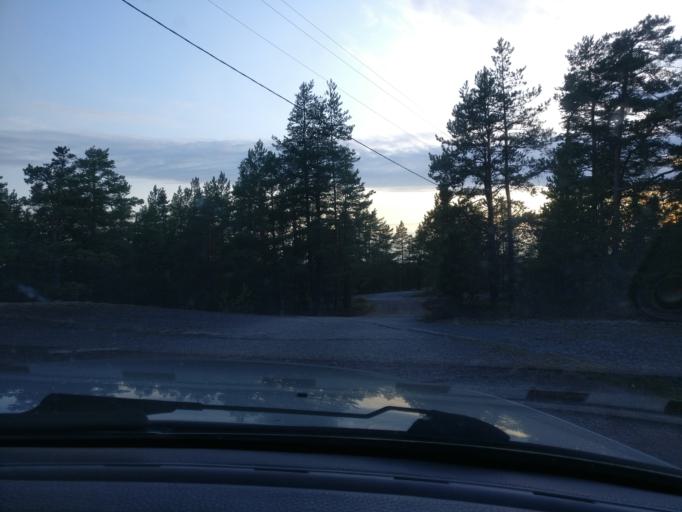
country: FI
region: Kymenlaakso
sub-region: Kotka-Hamina
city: Broby
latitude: 60.4710
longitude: 26.7734
